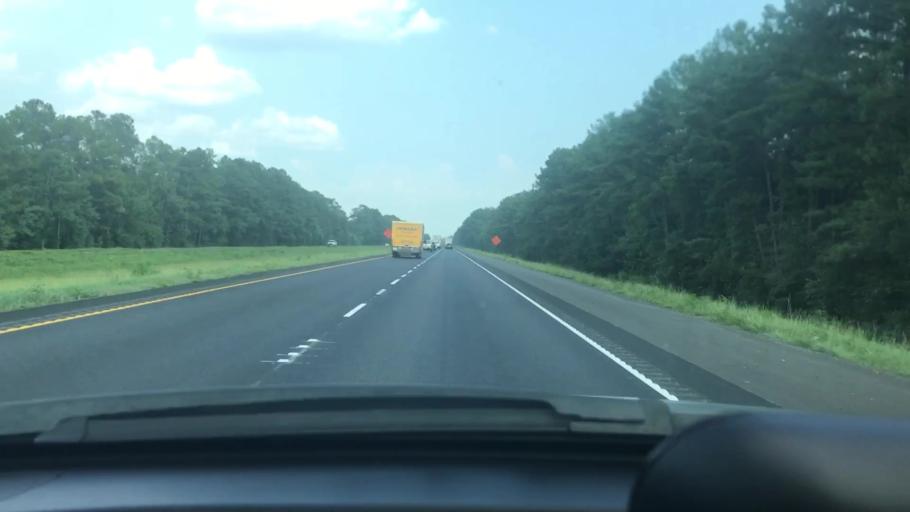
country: US
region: Louisiana
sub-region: Livingston Parish
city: Livingston
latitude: 30.4752
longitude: -90.6892
